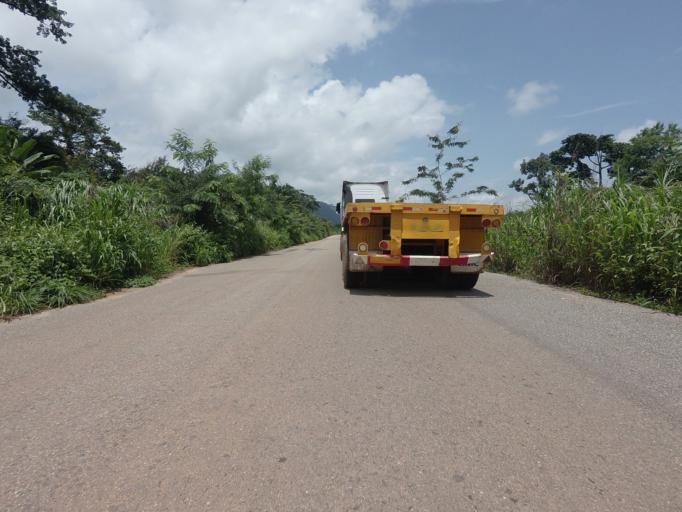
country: GH
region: Volta
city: Ho
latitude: 6.7817
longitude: 0.3657
